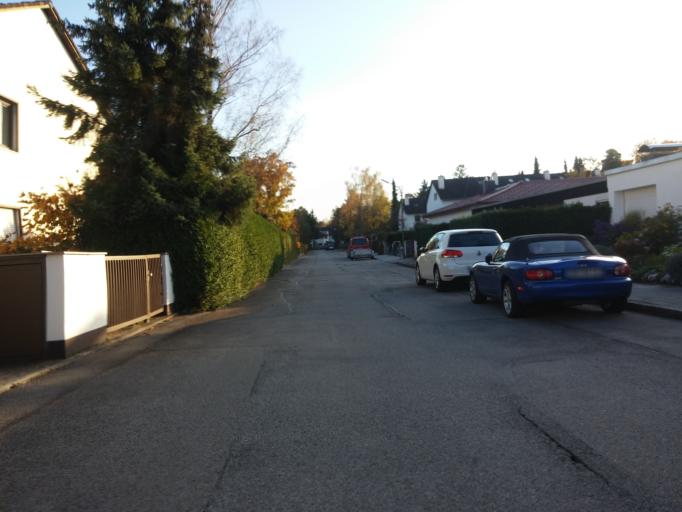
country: DE
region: Bavaria
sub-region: Upper Bavaria
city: Vaterstetten
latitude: 48.0951
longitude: 11.7832
